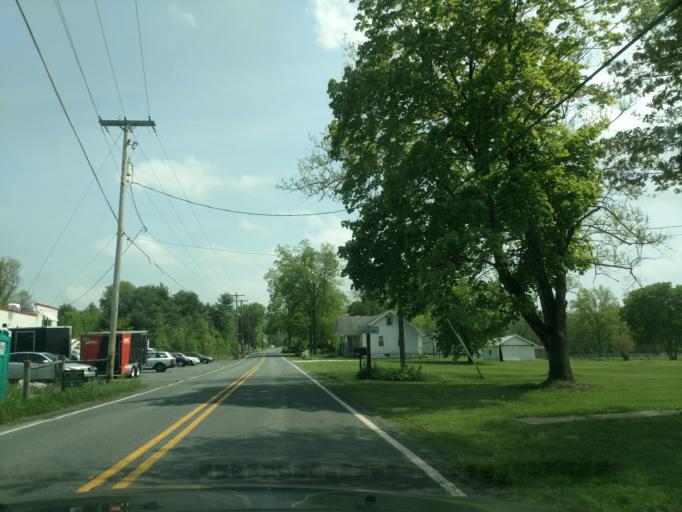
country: US
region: Pennsylvania
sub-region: Chester County
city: Elverson
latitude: 40.2087
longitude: -75.8402
